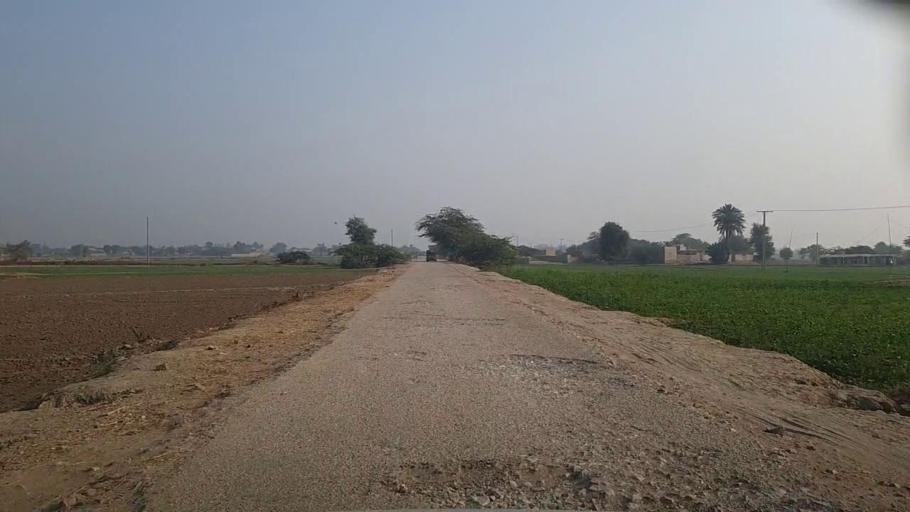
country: PK
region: Sindh
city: Kandiari
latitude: 27.0463
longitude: 68.4716
